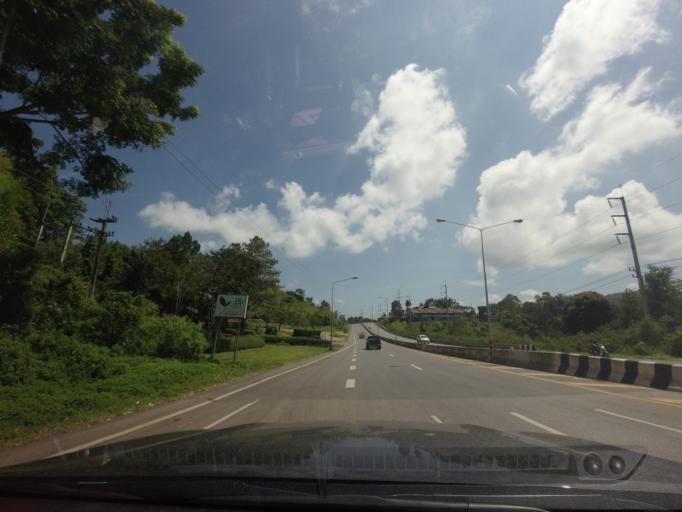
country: TH
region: Phetchabun
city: Khao Kho
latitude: 16.7697
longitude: 101.0504
